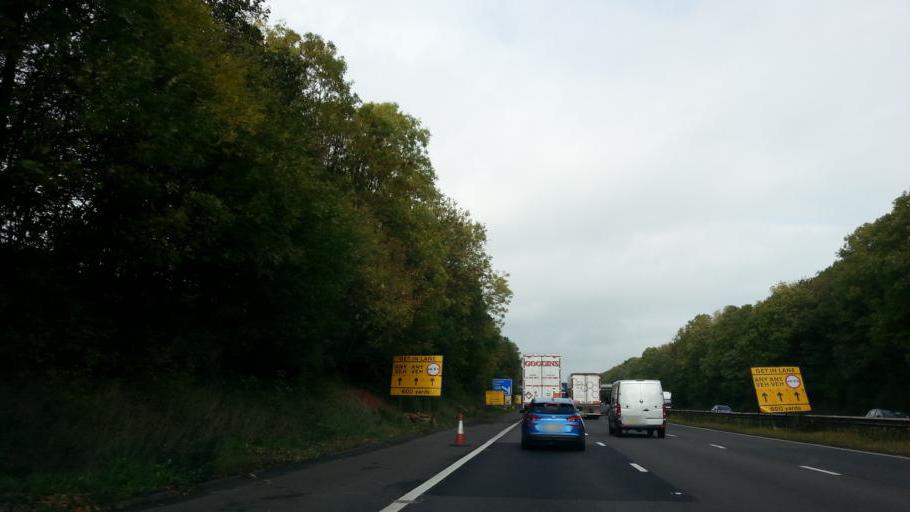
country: GB
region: England
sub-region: Staffordshire
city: Audley
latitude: 53.0520
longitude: -2.3311
